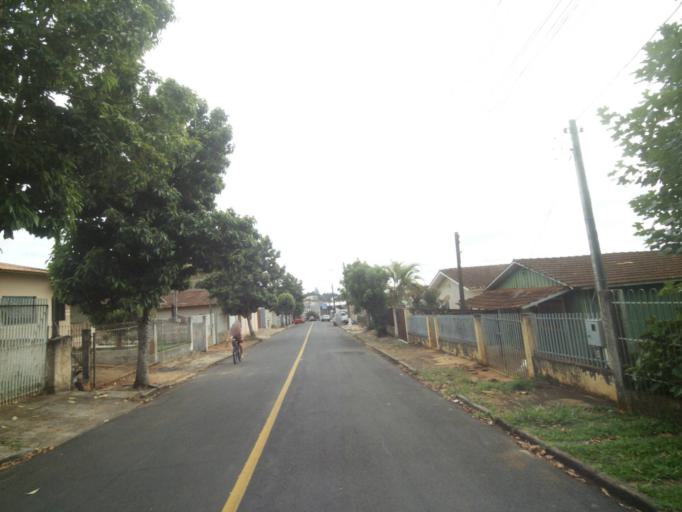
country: BR
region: Parana
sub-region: Telemaco Borba
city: Telemaco Borba
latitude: -24.3367
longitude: -50.6228
